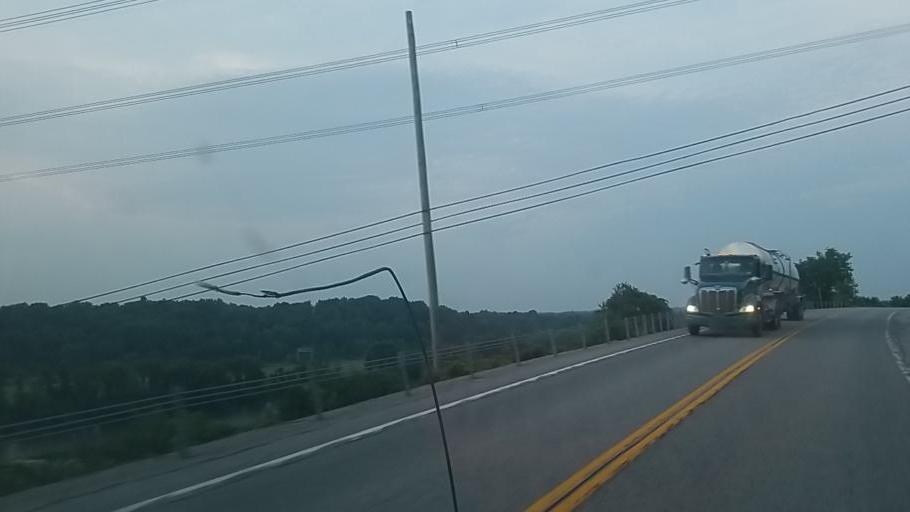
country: US
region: New York
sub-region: Montgomery County
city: Fonda
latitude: 42.9389
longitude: -74.4037
